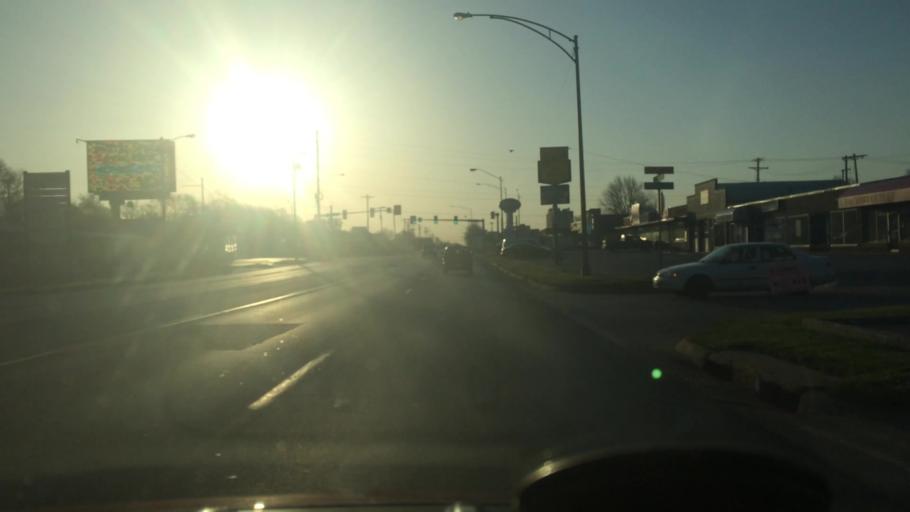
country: US
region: Missouri
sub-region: Greene County
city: Springfield
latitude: 37.1817
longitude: -93.2730
